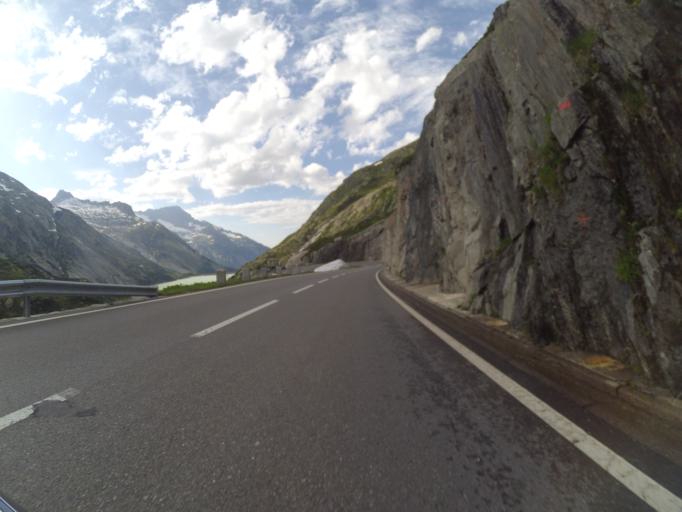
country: CH
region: Bern
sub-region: Interlaken-Oberhasli District
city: Meiringen
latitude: 46.5756
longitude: 8.3399
